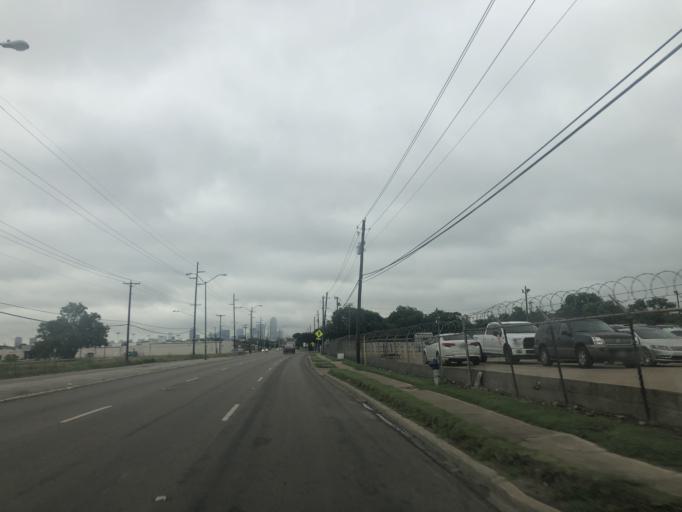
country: US
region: Texas
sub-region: Dallas County
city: Cockrell Hill
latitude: 32.7786
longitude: -96.8632
